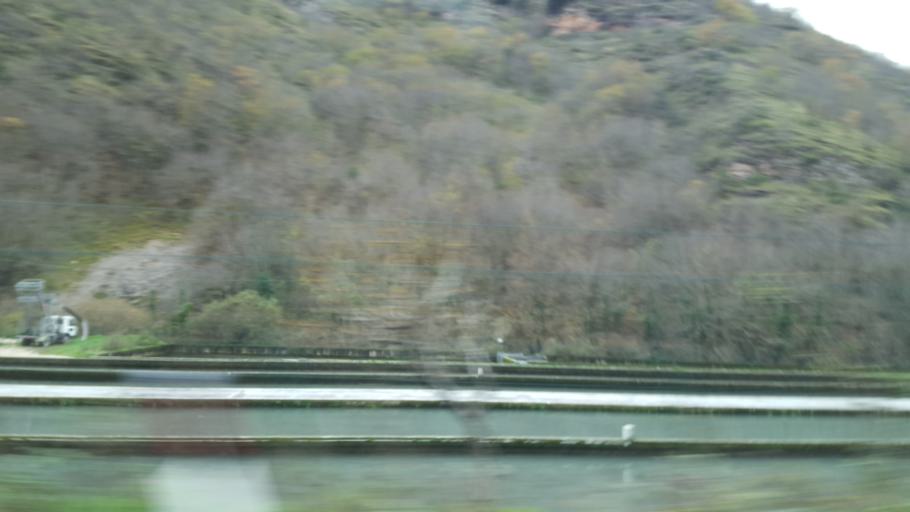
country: IT
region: The Marches
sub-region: Provincia di Macerata
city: Visso
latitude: 42.9251
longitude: 13.1026
